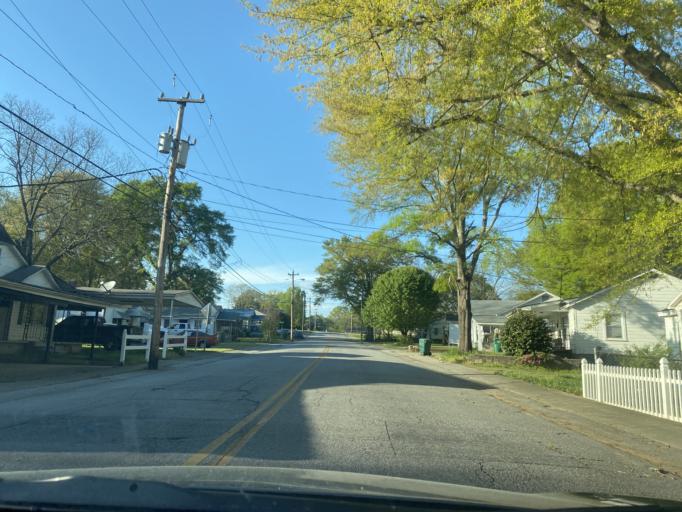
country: US
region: South Carolina
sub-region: Cherokee County
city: East Gaffney
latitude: 35.0724
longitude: -81.6354
